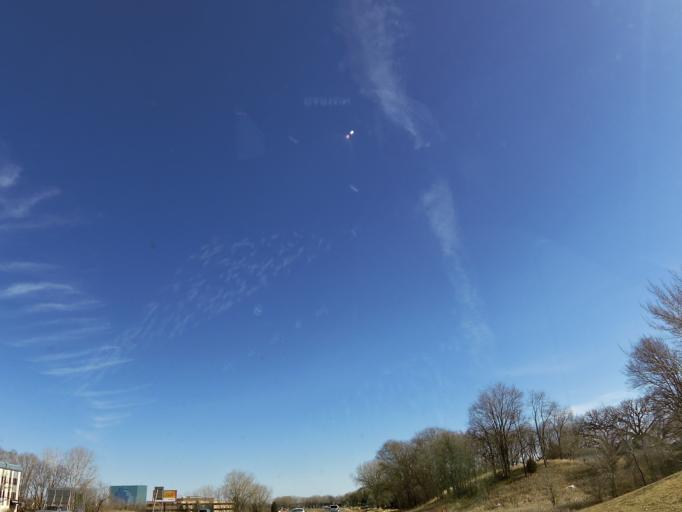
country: US
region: Minnesota
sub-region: Hennepin County
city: Plymouth
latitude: 44.9873
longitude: -93.4182
